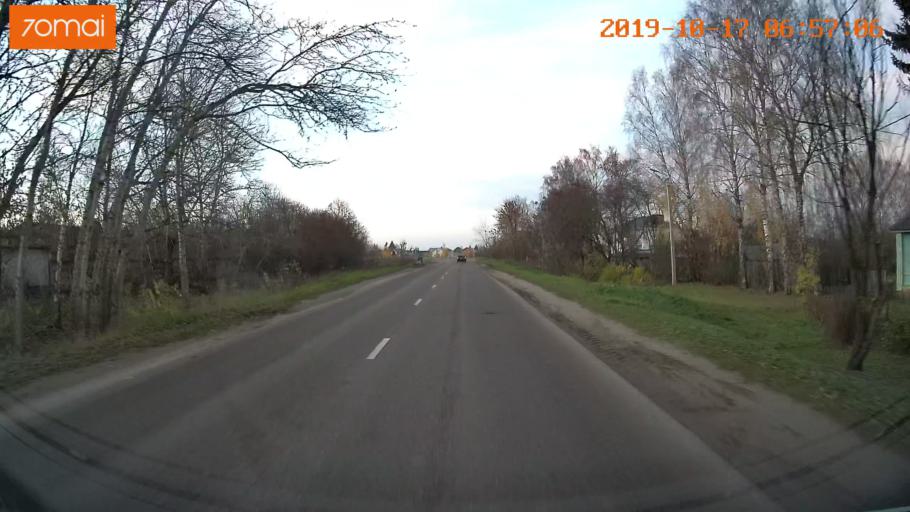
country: RU
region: Vladimir
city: Suzdal'
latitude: 56.4396
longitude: 40.4420
